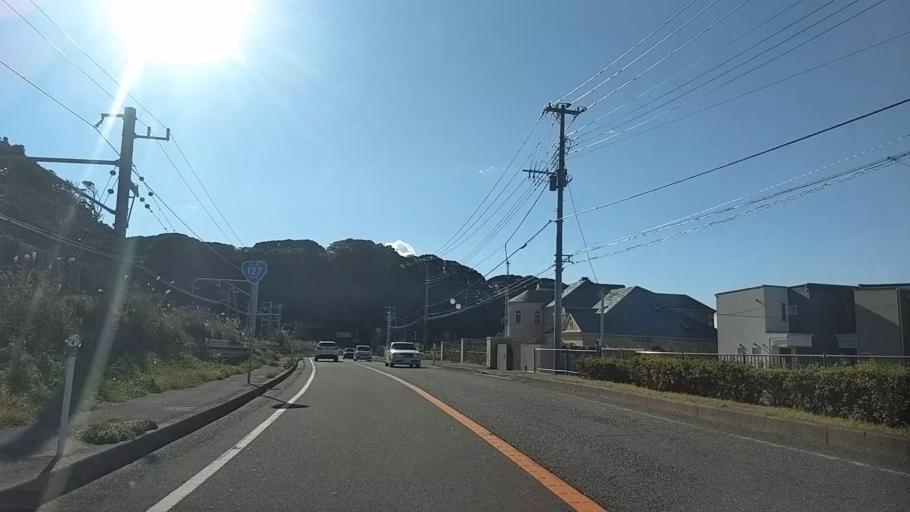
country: JP
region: Chiba
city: Futtsu
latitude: 35.1830
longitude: 139.8189
